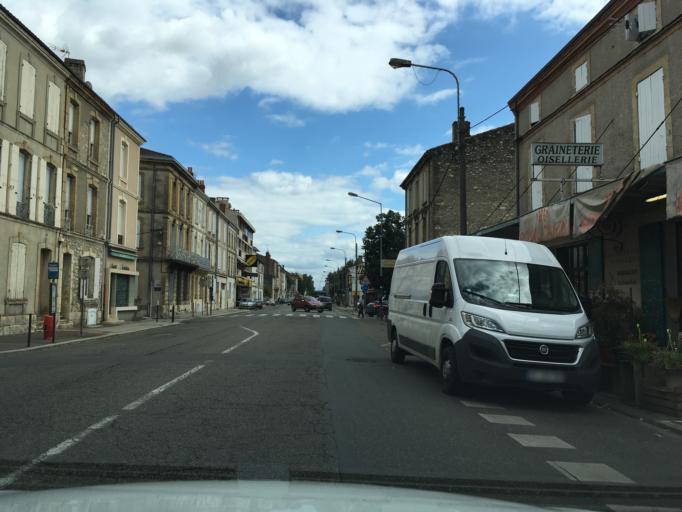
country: FR
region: Aquitaine
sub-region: Departement du Lot-et-Garonne
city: Agen
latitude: 44.2041
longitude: 0.6273
